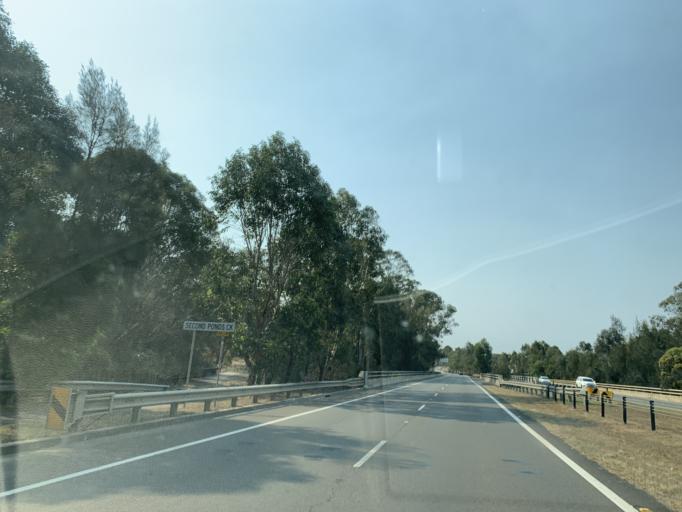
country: AU
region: New South Wales
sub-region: Blacktown
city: Rouse Hill
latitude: -33.6790
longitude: 150.9134
